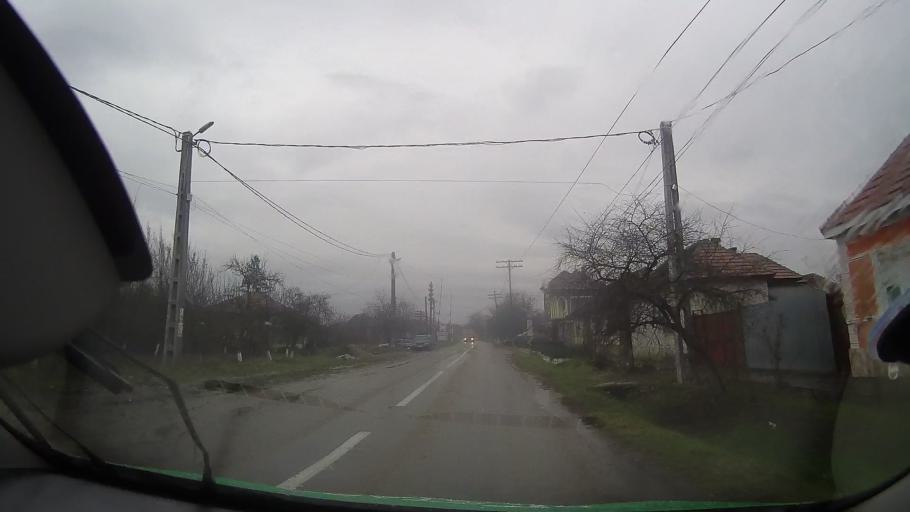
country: RO
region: Bihor
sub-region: Comuna Holod
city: Holod
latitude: 46.7820
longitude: 22.1339
